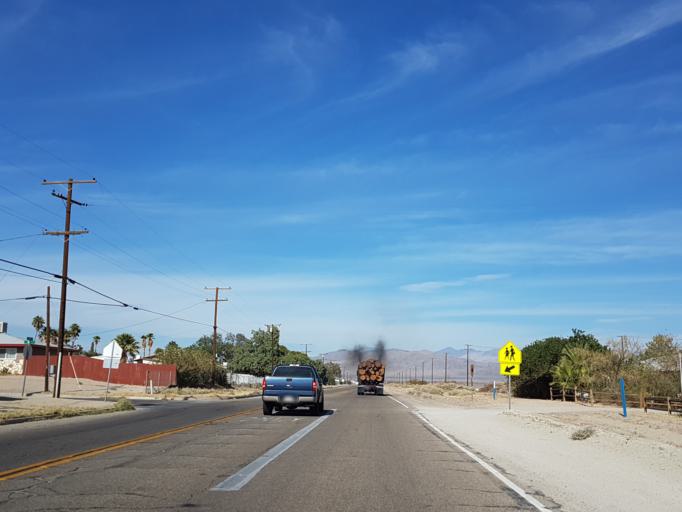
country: US
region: California
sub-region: San Bernardino County
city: Searles Valley
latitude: 35.7907
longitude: -117.3585
